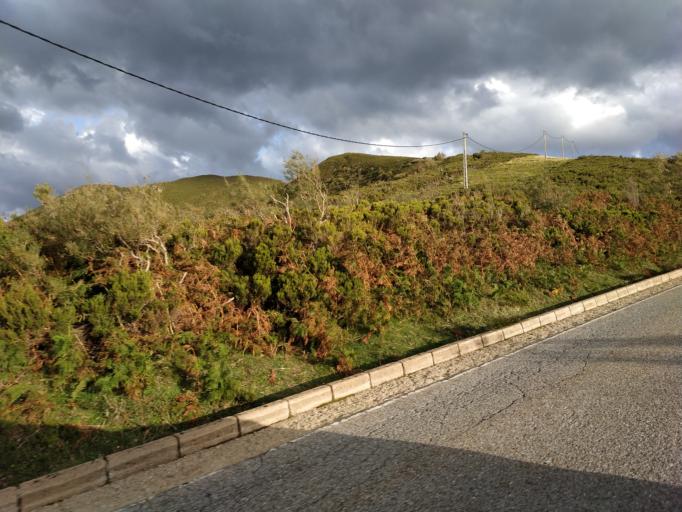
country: ES
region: Castille and Leon
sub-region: Provincia de Leon
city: Candin
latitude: 42.8731
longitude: -6.8227
